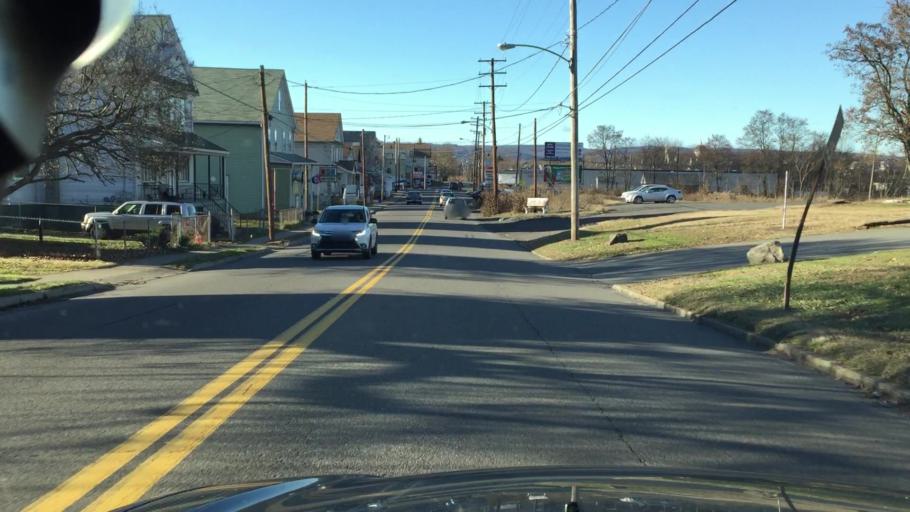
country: US
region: Pennsylvania
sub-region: Luzerne County
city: Ashley
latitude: 41.2230
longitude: -75.8864
